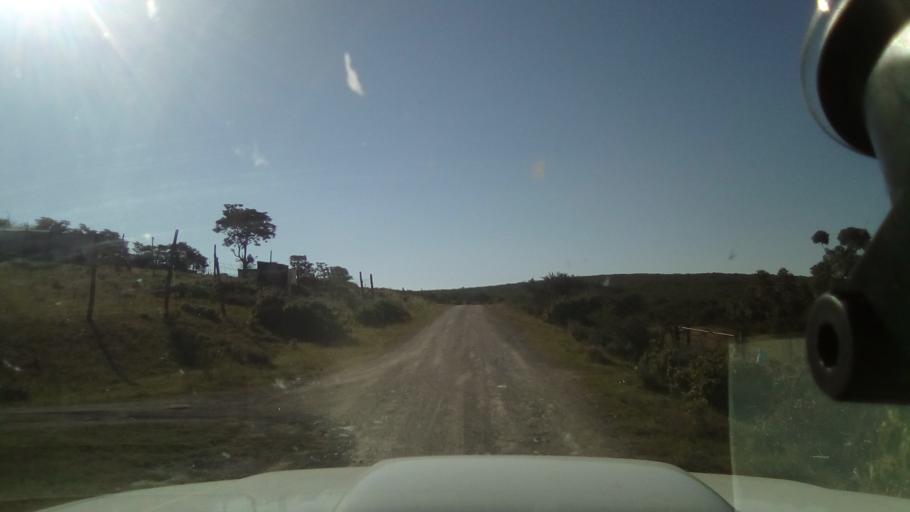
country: ZA
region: Eastern Cape
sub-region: Buffalo City Metropolitan Municipality
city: Bhisho
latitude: -32.7973
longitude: 27.3421
